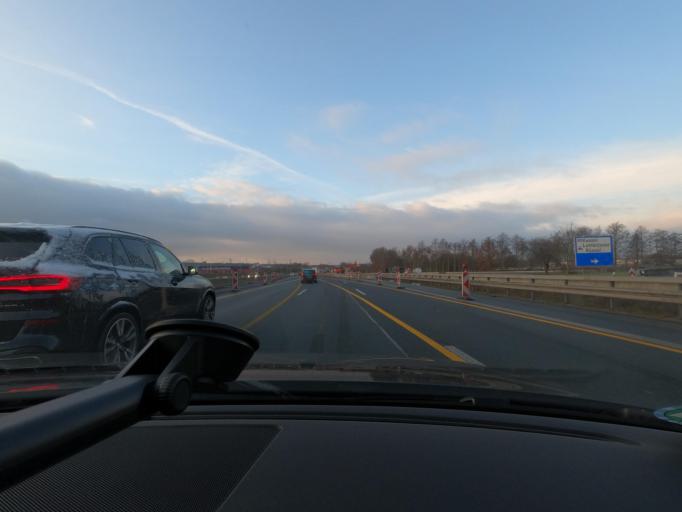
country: DE
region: Hesse
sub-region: Regierungsbezirk Kassel
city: Lohfelden
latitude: 51.2756
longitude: 9.5281
